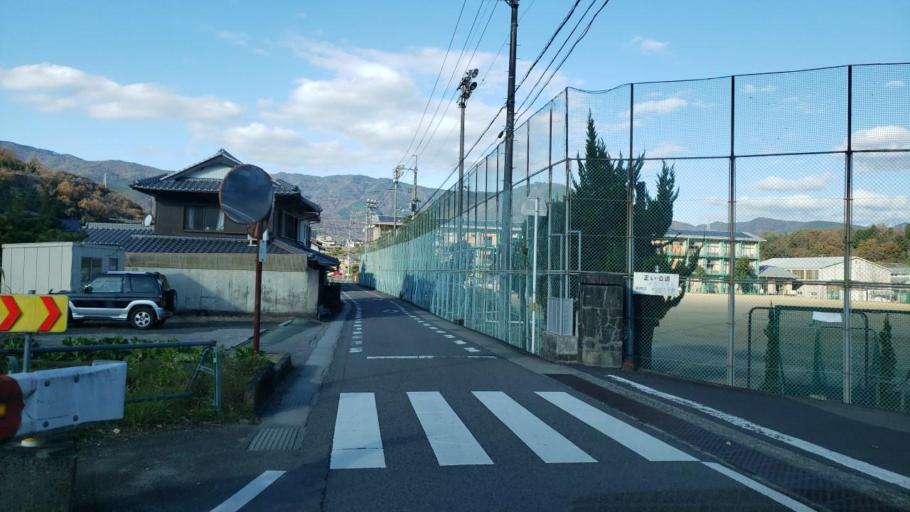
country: JP
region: Tokushima
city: Wakimachi
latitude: 34.0310
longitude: 134.0295
